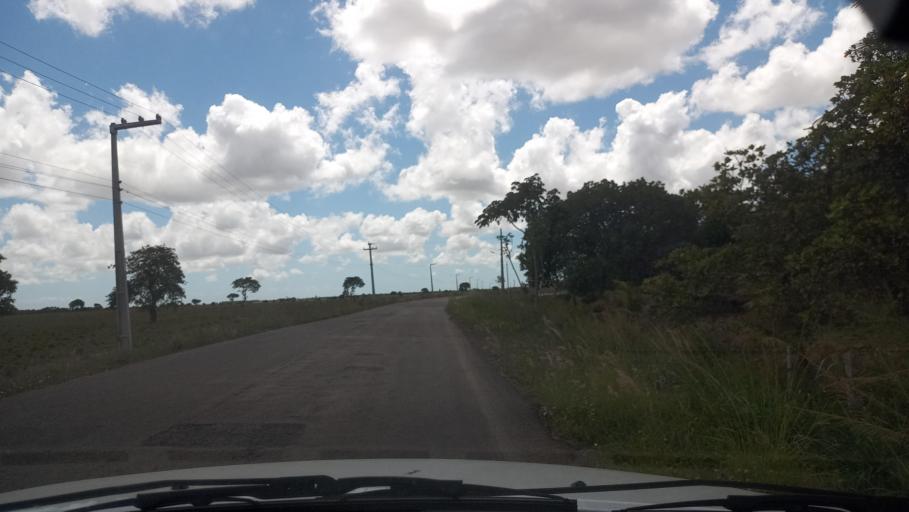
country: BR
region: Rio Grande do Norte
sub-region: Brejinho
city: Brejinho
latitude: -6.0408
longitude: -35.4042
